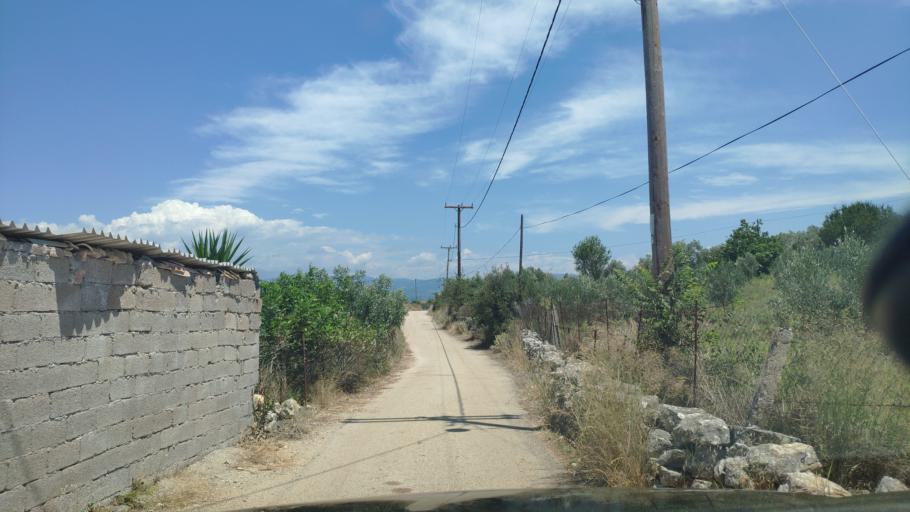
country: GR
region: West Greece
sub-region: Nomos Aitolias kai Akarnanias
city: Amfilochia
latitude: 38.9002
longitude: 21.0996
